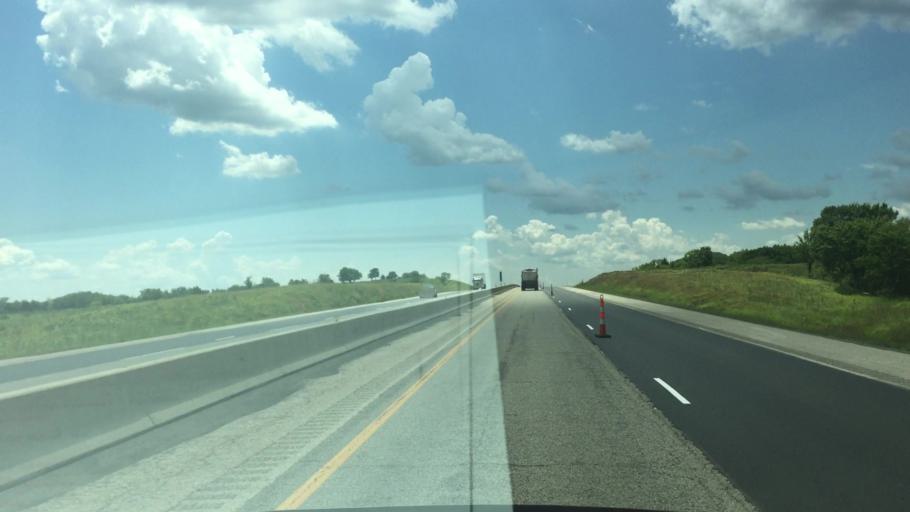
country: US
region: Kansas
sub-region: Shawnee County
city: Auburn
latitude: 38.8740
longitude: -95.8307
